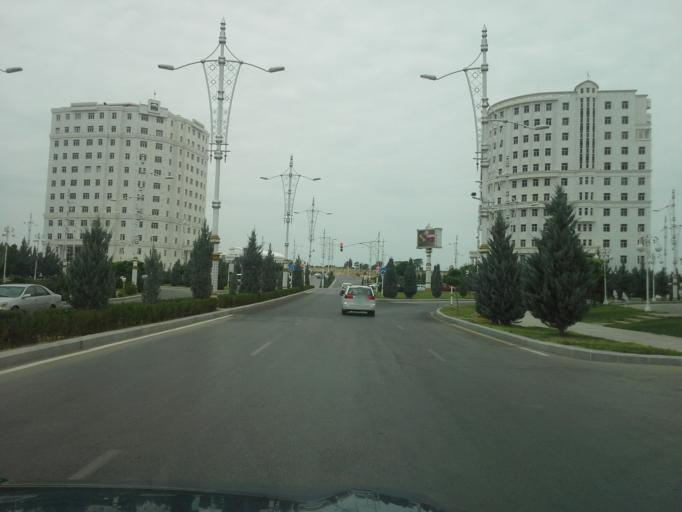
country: TM
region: Ahal
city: Ashgabat
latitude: 37.9203
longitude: 58.3603
